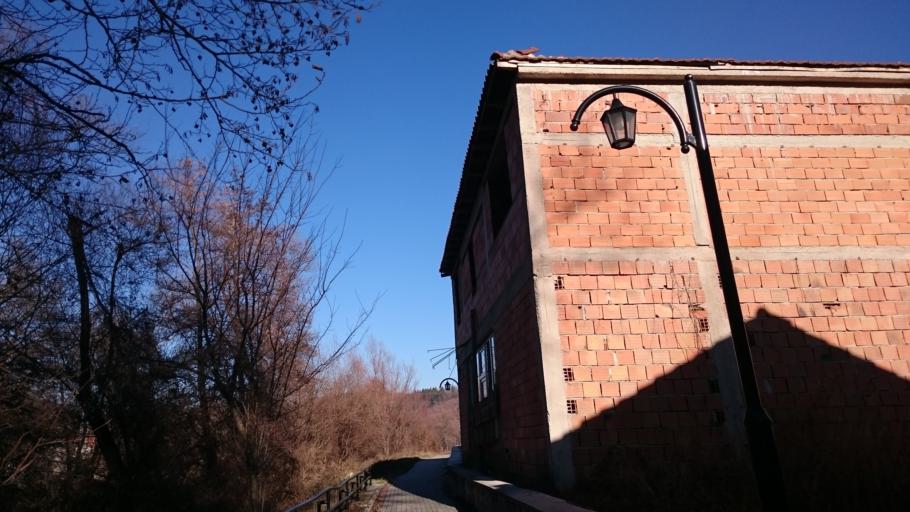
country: MK
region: Makedonski Brod
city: Makedonski Brod
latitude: 41.5083
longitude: 21.2171
